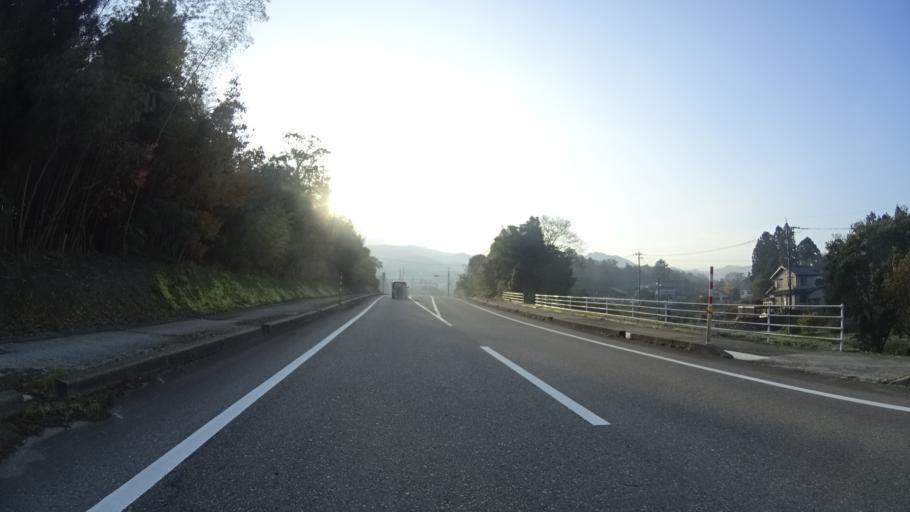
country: JP
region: Ishikawa
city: Nanao
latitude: 37.0267
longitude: 136.9754
